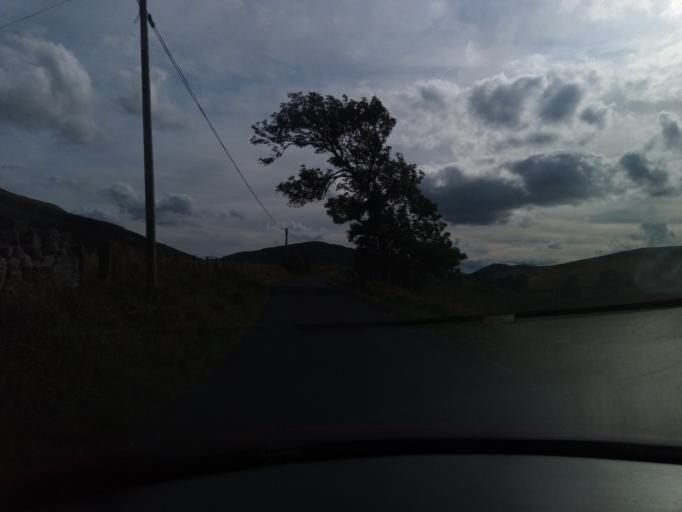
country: GB
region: Scotland
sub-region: The Scottish Borders
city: Kelso
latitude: 55.4754
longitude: -2.3529
